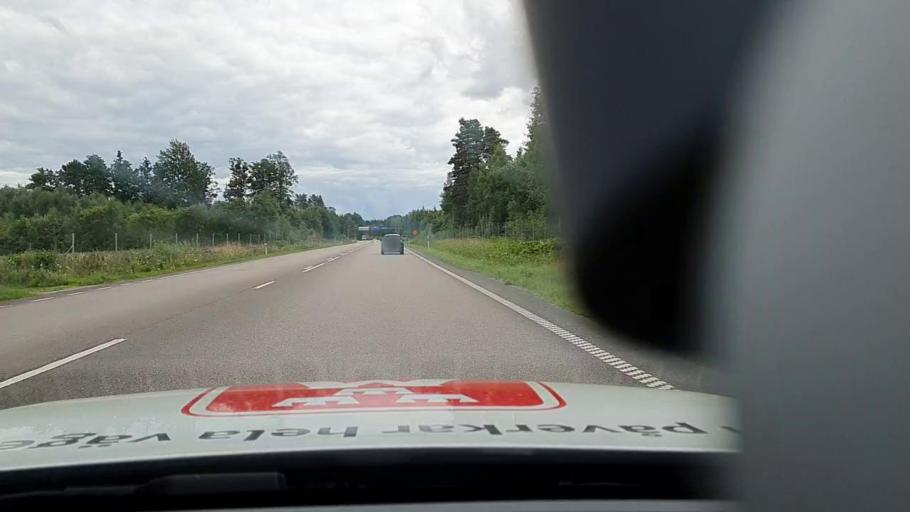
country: SE
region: Vaestra Goetaland
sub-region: Lidkopings Kommun
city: Vinninga
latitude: 58.4511
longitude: 13.2411
